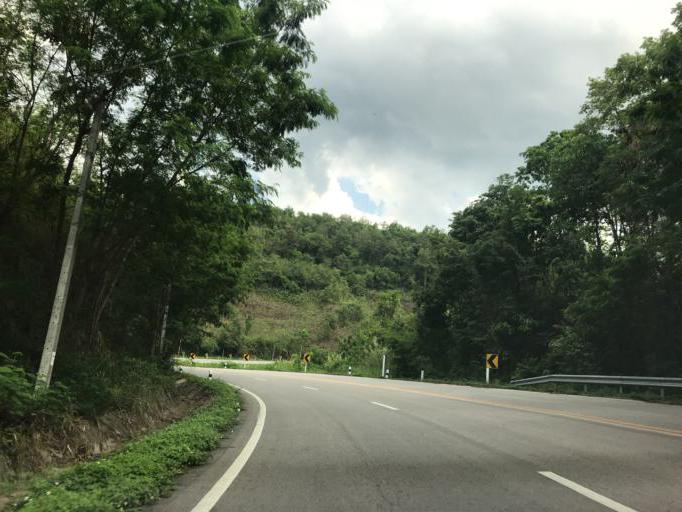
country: TH
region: Phayao
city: Phayao
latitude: 19.0882
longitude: 99.8099
